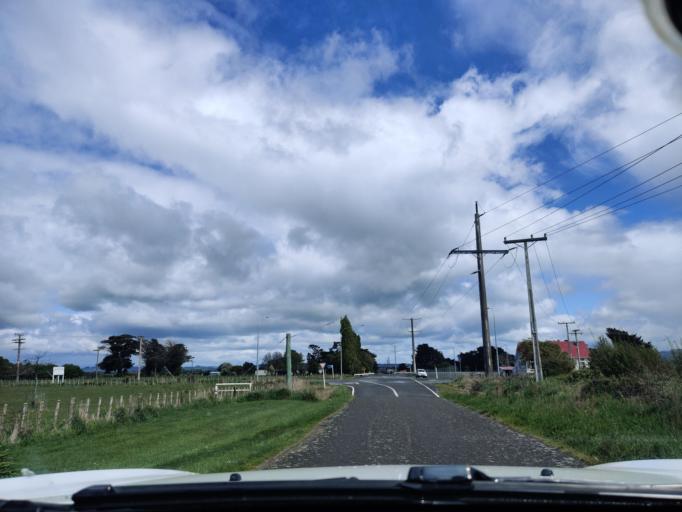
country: NZ
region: Manawatu-Wanganui
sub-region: Palmerston North City
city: Palmerston North
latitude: -40.3170
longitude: 175.8565
